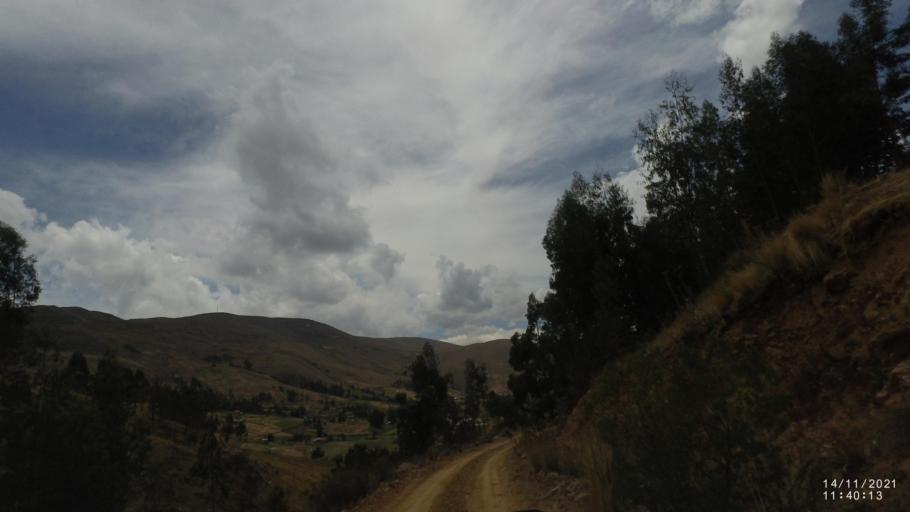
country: BO
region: Cochabamba
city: Colomi
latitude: -17.3511
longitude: -65.9970
